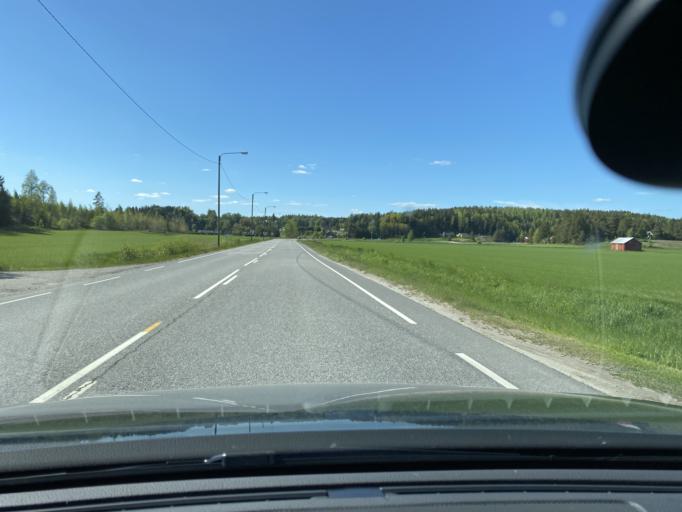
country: FI
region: Varsinais-Suomi
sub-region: Turku
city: Sauvo
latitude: 60.3510
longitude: 22.6761
